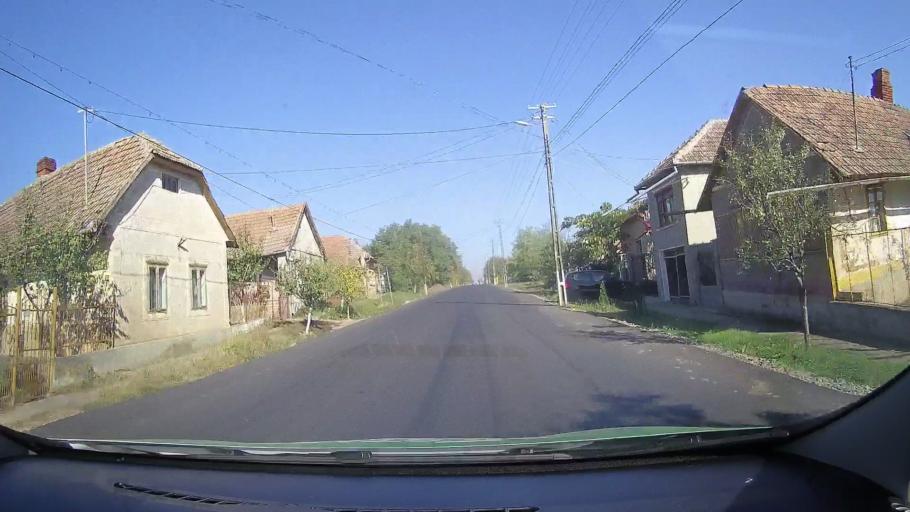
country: RO
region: Satu Mare
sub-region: Comuna Tiream
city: Tiream
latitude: 47.6189
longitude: 22.4684
